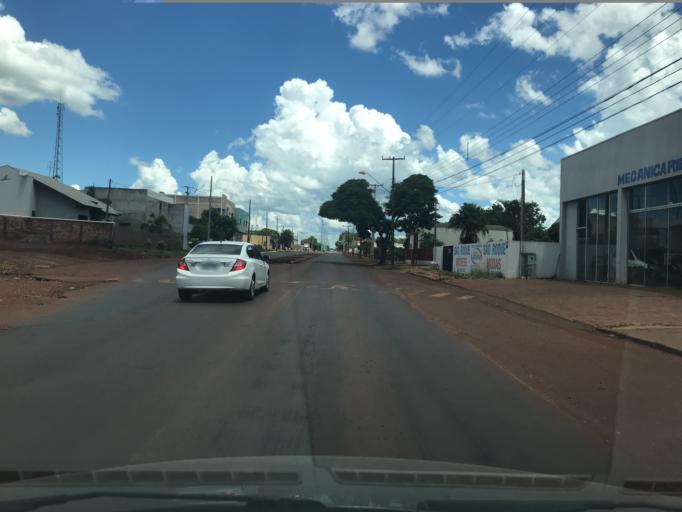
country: BR
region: Parana
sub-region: Palotina
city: Palotina
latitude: -24.2680
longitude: -53.8417
